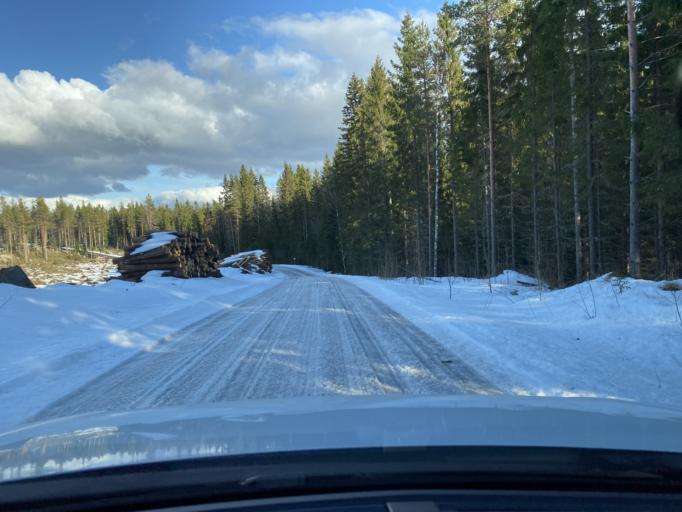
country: FI
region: Pirkanmaa
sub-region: Lounais-Pirkanmaa
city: Mouhijaervi
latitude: 61.4555
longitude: 22.9375
